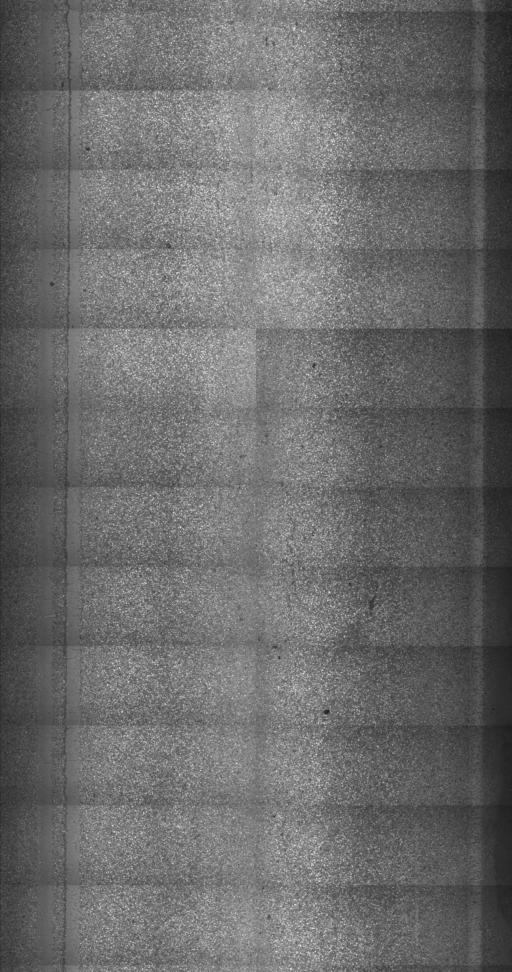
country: US
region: Vermont
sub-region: Rutland County
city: Fair Haven
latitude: 43.5870
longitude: -73.2652
